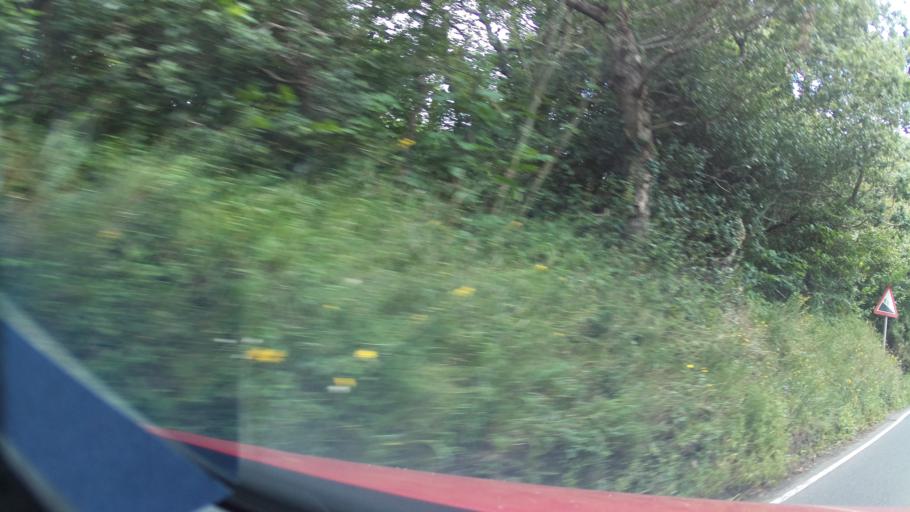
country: GB
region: England
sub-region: Devon
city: Bishopsteignton
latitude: 50.5686
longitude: -3.5176
